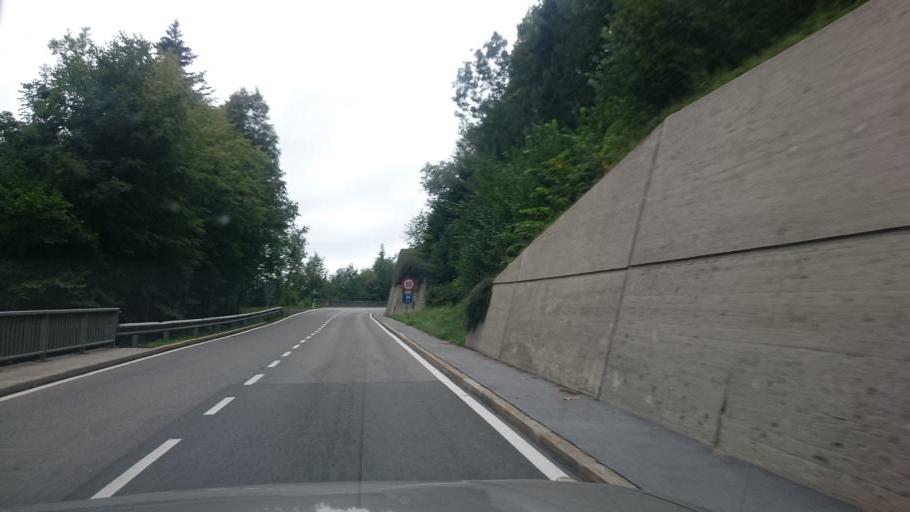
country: AT
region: Vorarlberg
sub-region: Politischer Bezirk Bregenz
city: Bildstein
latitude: 47.4250
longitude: 9.7795
